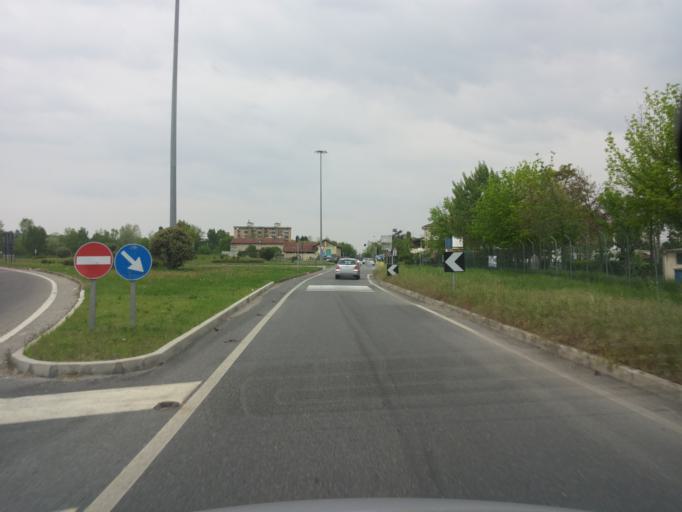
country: IT
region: Piedmont
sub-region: Provincia di Alessandria
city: Casale Monferrato
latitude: 45.1145
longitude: 8.4515
